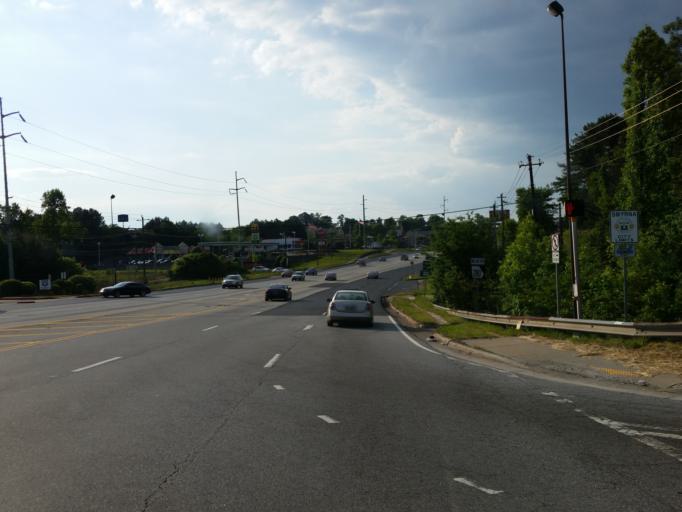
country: US
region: Georgia
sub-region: Cobb County
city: Vinings
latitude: 33.8258
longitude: -84.4900
